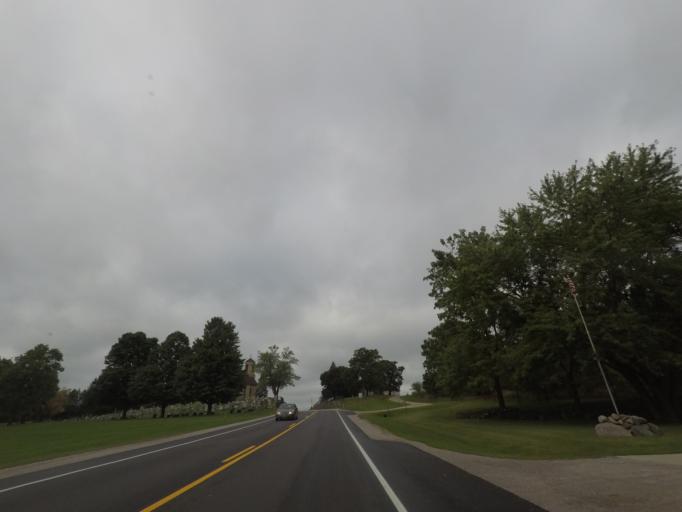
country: US
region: Wisconsin
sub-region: Jefferson County
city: Jefferson
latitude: 43.0062
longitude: -88.7772
